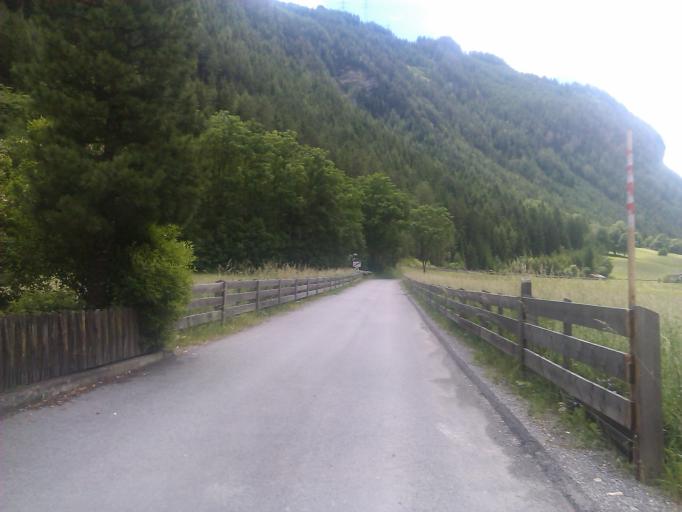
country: AT
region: Tyrol
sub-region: Politischer Bezirk Landeck
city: Fiss
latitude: 47.0288
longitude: 10.6266
